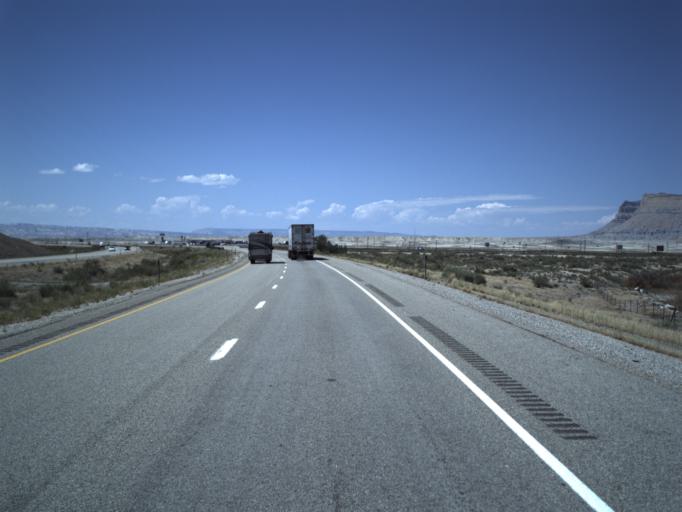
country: US
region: Utah
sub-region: Carbon County
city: East Carbon City
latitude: 38.9889
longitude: -110.1699
